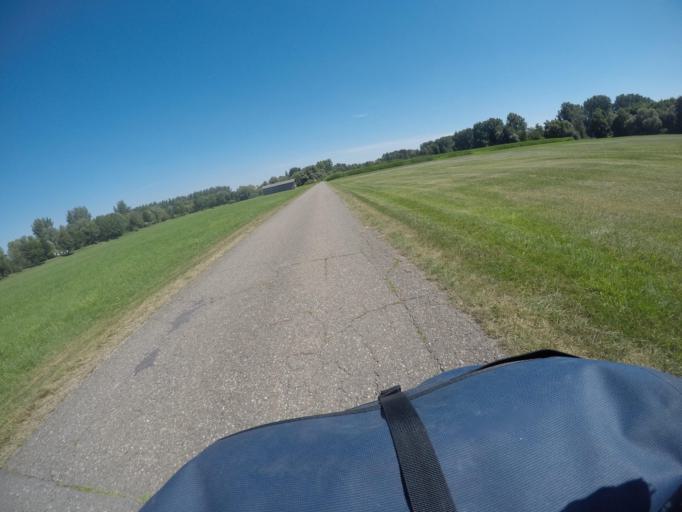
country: DE
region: Baden-Wuerttemberg
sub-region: Tuebingen Region
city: Neufra
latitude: 48.1304
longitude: 9.4629
